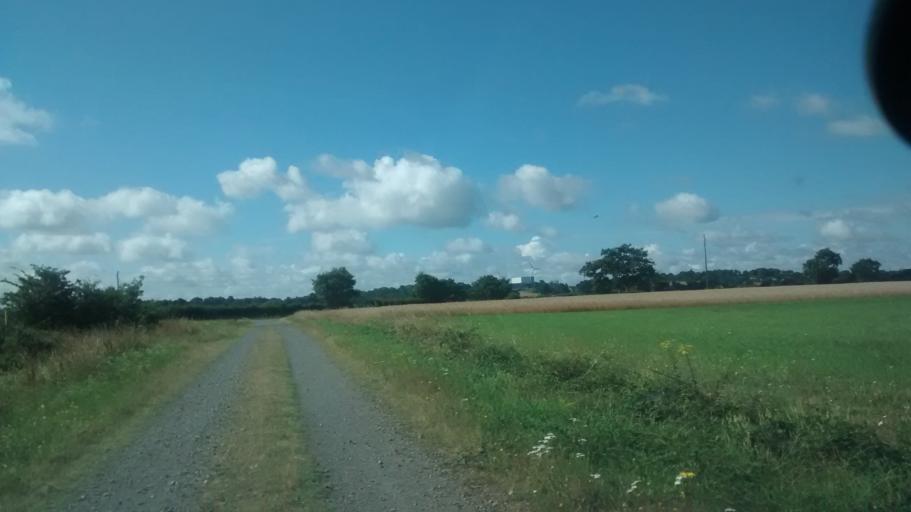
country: FR
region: Brittany
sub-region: Departement d'Ille-et-Vilaine
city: La Dominelais
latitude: 47.7692
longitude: -1.7152
